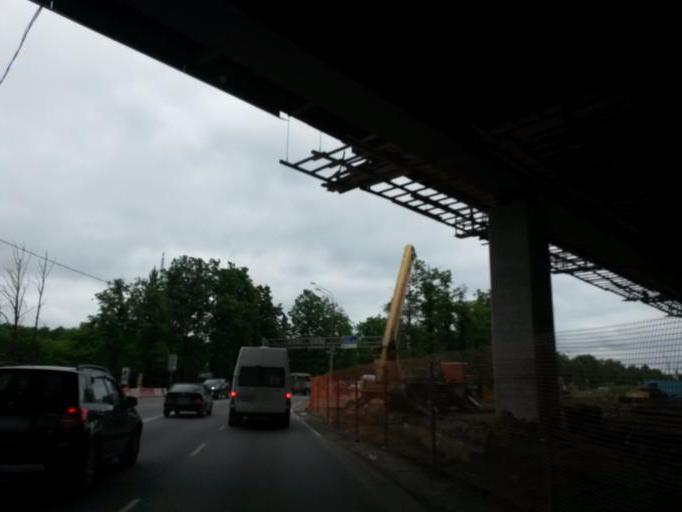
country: RU
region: Moskovskaya
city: Klimovsk
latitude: 55.3839
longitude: 37.5377
